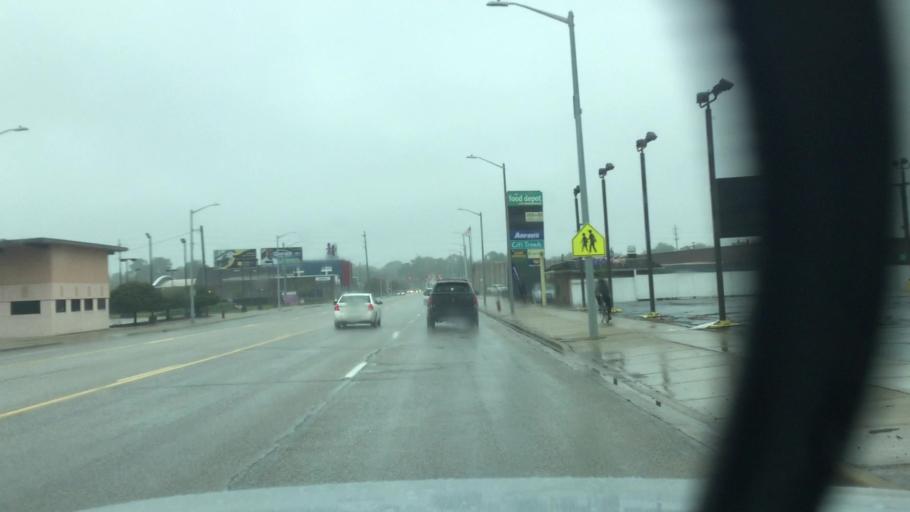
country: US
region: Michigan
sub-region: Saginaw County
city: Saginaw
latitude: 43.4342
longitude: -83.9436
